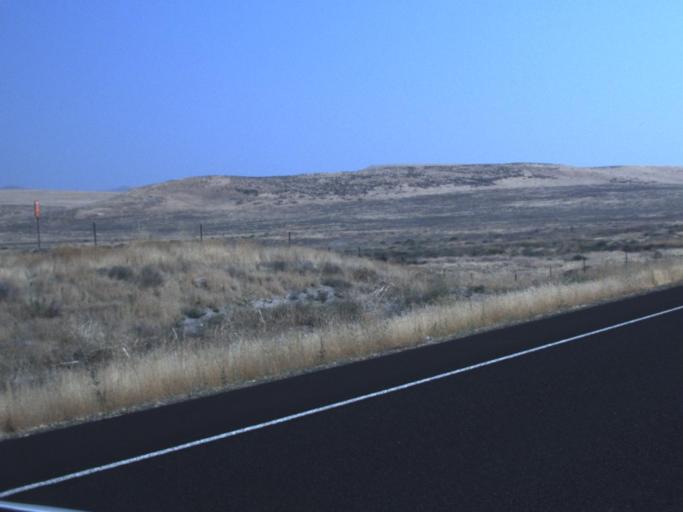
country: US
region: Washington
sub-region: Yakima County
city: Zillah
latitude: 46.5058
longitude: -120.1649
